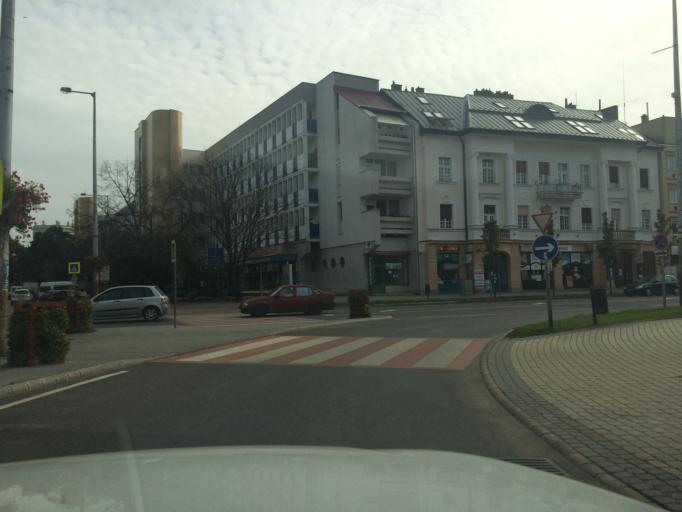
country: HU
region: Szabolcs-Szatmar-Bereg
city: Nyiregyhaza
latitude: 47.9539
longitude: 21.7153
